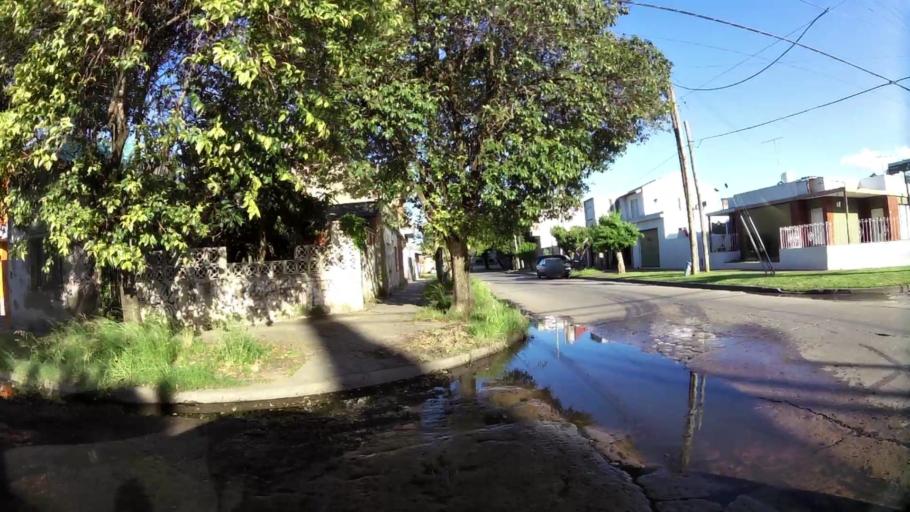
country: AR
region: Buenos Aires
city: Ituzaingo
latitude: -34.6899
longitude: -58.6399
